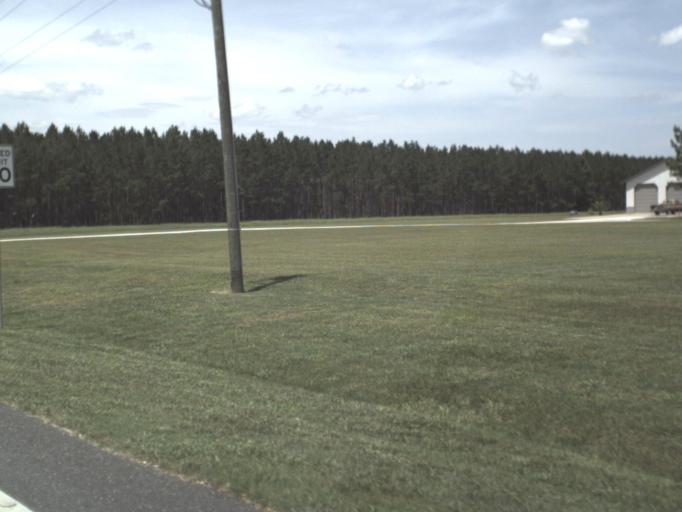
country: US
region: Florida
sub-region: Gilchrist County
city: Trenton
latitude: 29.8346
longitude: -82.8674
